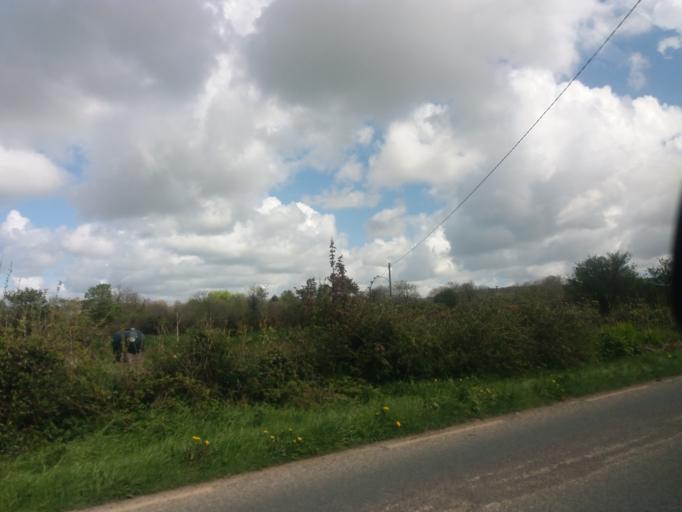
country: IE
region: Leinster
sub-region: Loch Garman
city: Loch Garman
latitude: 52.2883
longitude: -6.6163
